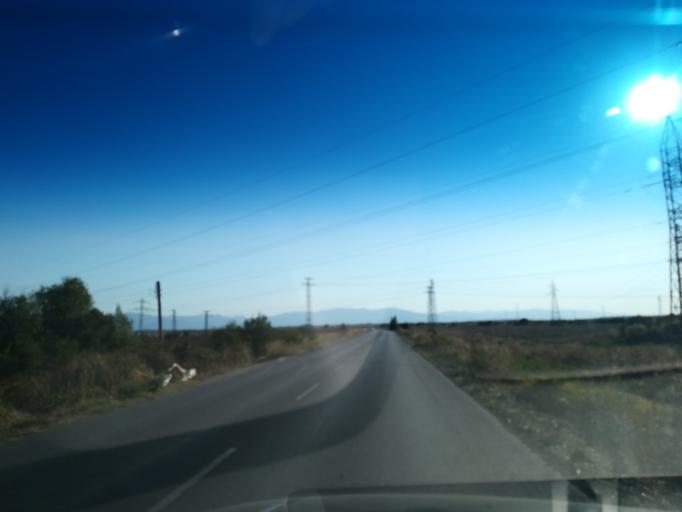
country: BG
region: Stara Zagora
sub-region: Obshtina Chirpan
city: Chirpan
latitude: 42.1063
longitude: 25.2141
